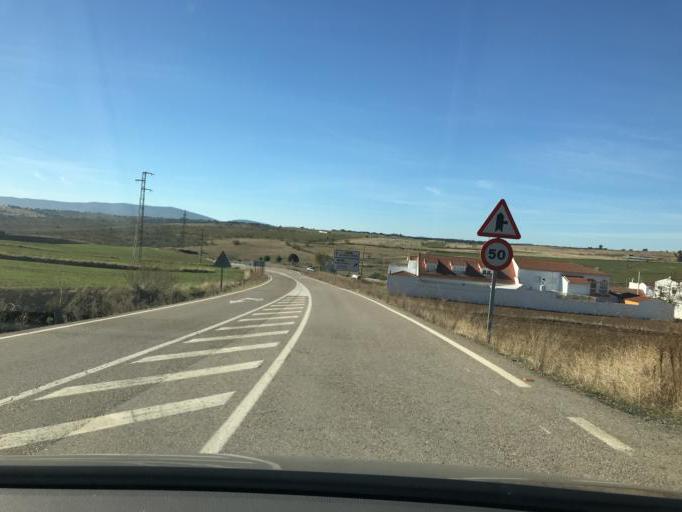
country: ES
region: Extremadura
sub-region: Provincia de Badajoz
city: Valverde de Llerena
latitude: 38.2111
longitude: -5.8200
